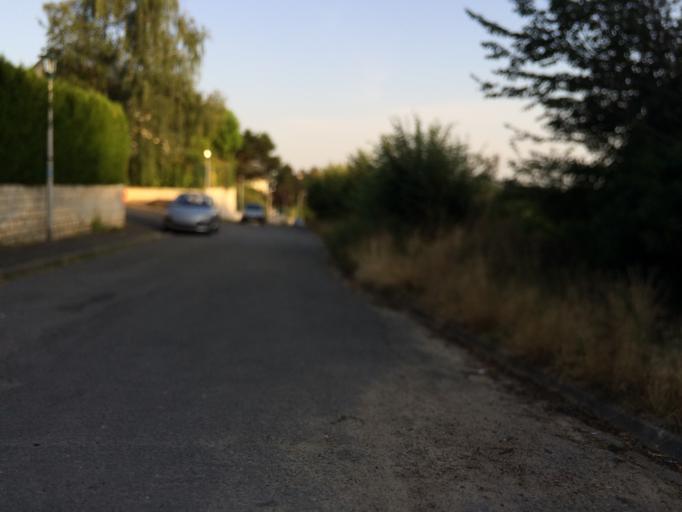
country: FR
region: Ile-de-France
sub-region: Departement de l'Essonne
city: Verrieres-le-Buisson
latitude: 48.7427
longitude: 2.2506
